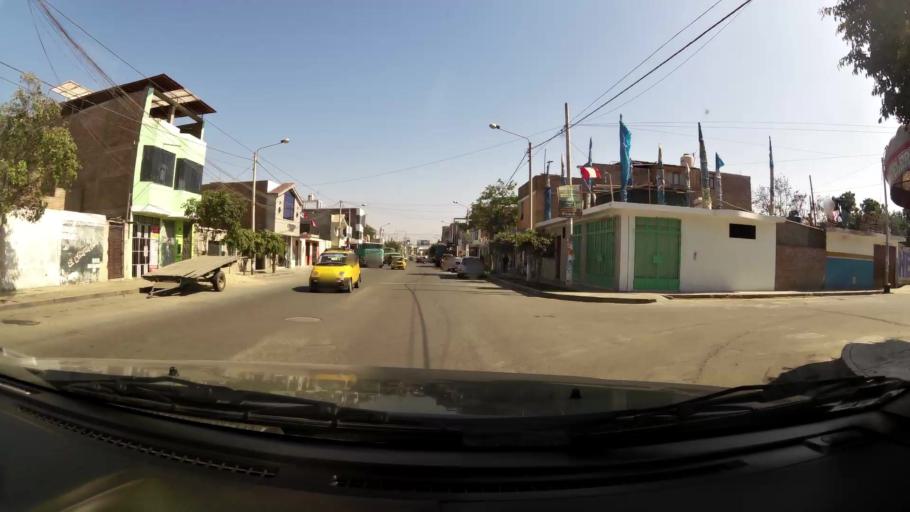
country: PE
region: Ica
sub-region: Provincia de Ica
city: La Tinguina
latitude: -14.0498
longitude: -75.7032
